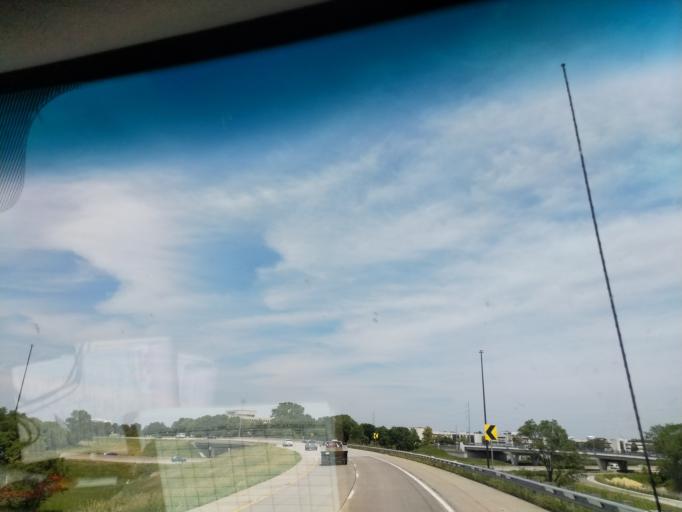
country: US
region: Iowa
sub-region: Polk County
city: Clive
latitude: 41.5905
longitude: -93.7742
